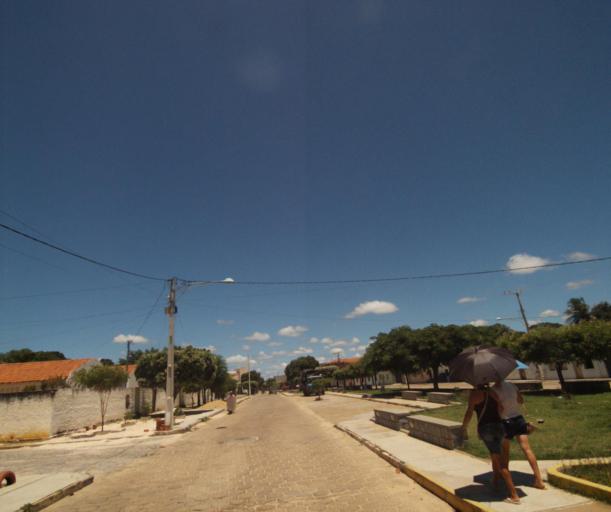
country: BR
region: Bahia
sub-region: Carinhanha
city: Carinhanha
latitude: -14.3050
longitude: -43.7689
